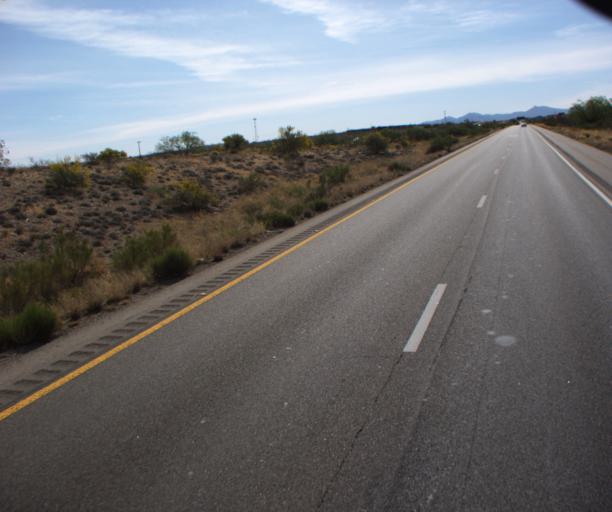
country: US
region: Arizona
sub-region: Pima County
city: Vail
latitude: 32.0188
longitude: -110.7083
